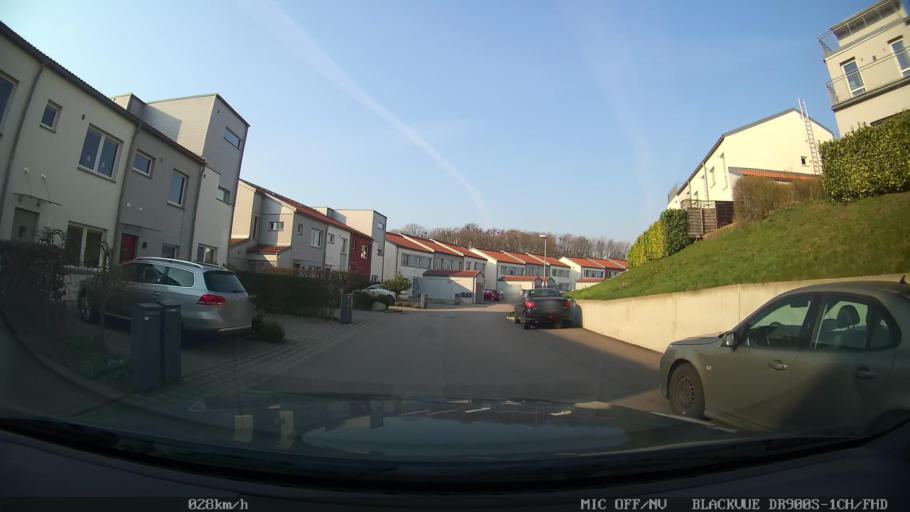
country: SE
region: Skane
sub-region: Ystads Kommun
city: Ystad
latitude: 55.4381
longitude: 13.8282
